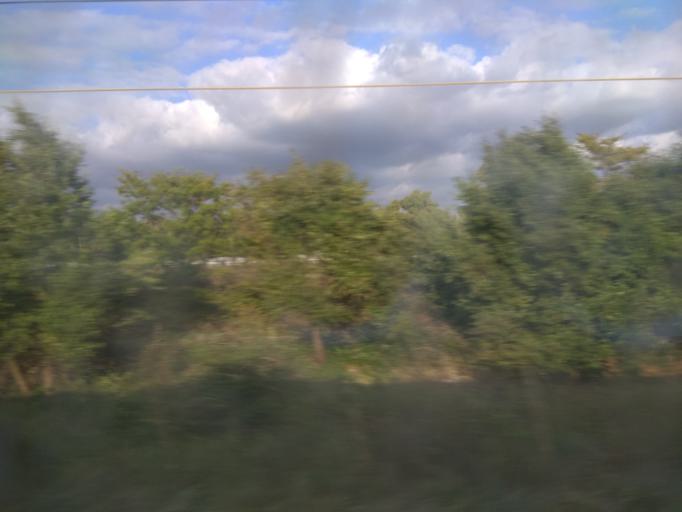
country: IT
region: Latium
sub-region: Citta metropolitana di Roma Capitale
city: Maccarese
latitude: 41.9011
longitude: 12.2153
